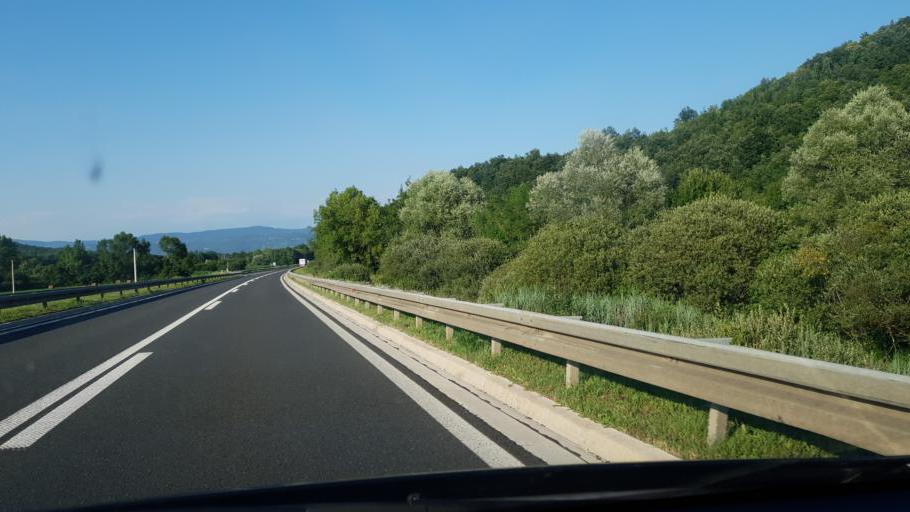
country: HR
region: Istarska
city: Pazin
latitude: 45.2871
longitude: 14.0307
